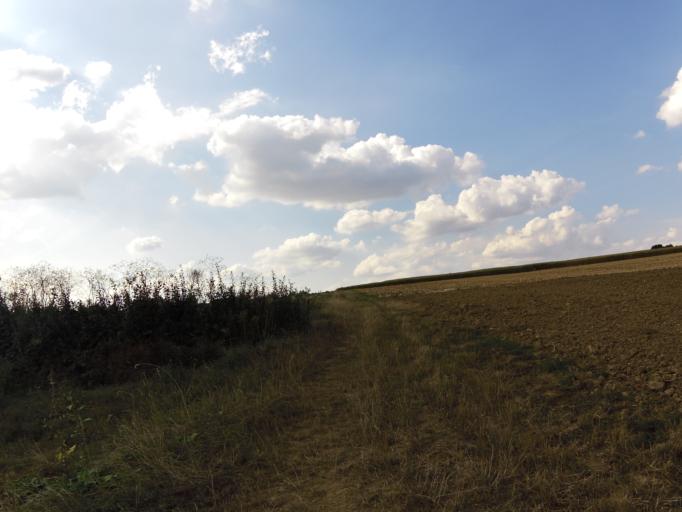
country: DE
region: Bavaria
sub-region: Regierungsbezirk Unterfranken
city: Estenfeld
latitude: 49.8210
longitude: 9.9983
